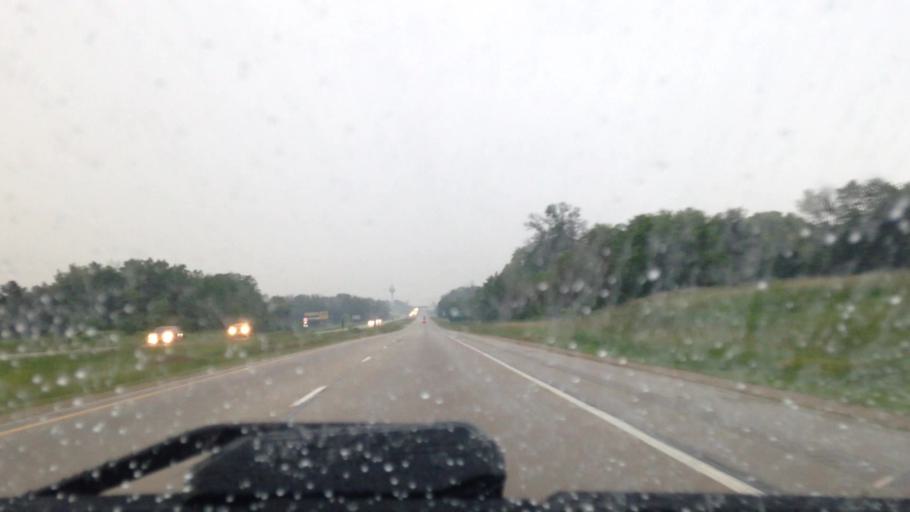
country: US
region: Wisconsin
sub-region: Washington County
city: Slinger
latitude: 43.4098
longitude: -88.3284
